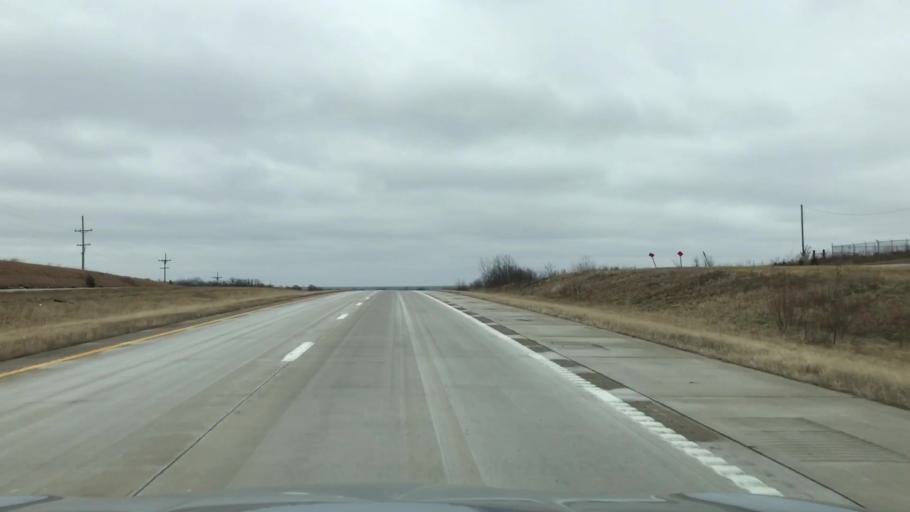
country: US
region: Missouri
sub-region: Livingston County
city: Chillicothe
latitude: 39.7394
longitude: -93.6593
